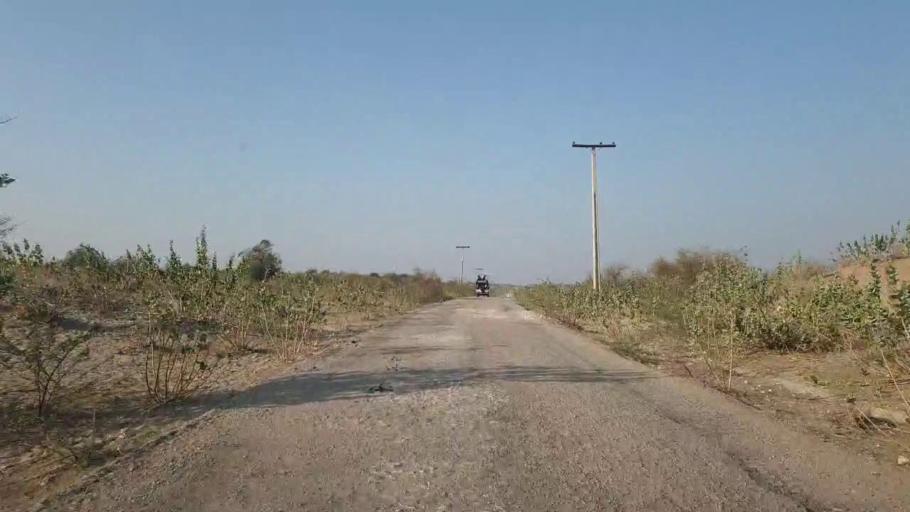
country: PK
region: Sindh
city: Chor
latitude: 25.6105
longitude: 69.8377
